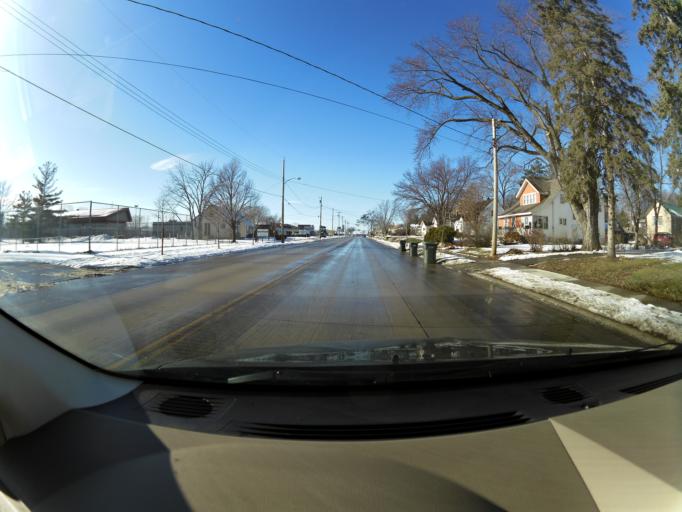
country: US
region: Minnesota
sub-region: Olmsted County
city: Rochester
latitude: 44.0310
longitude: -92.4740
